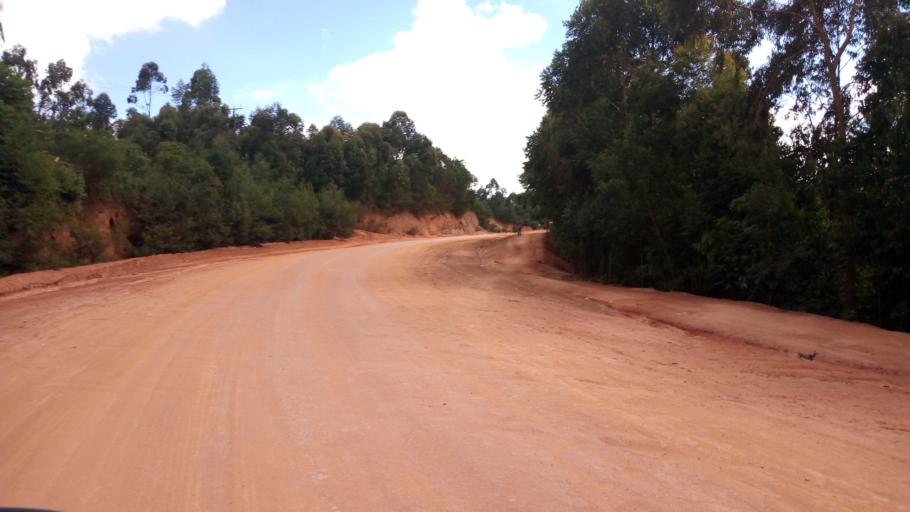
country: KE
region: Makueni
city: Wote
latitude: -1.6551
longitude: 37.4590
